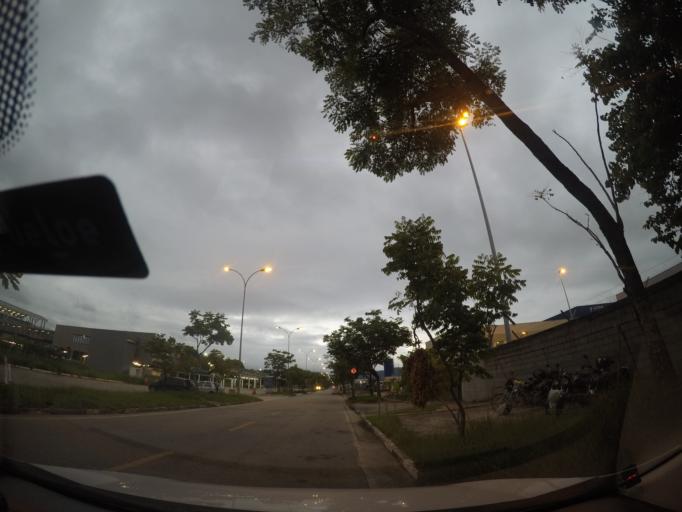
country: BR
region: Sao Paulo
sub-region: Guarulhos
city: Guarulhos
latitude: -23.4335
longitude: -46.4921
